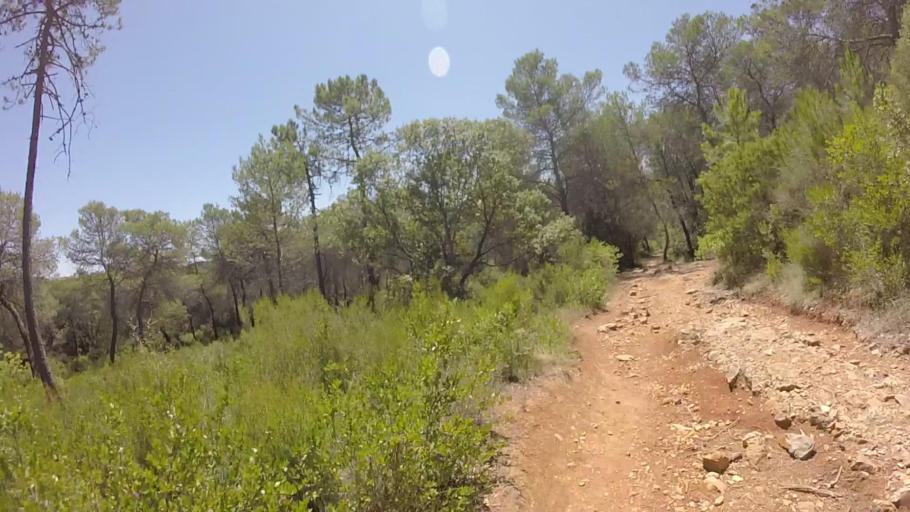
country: FR
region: Provence-Alpes-Cote d'Azur
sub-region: Departement des Alpes-Maritimes
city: Vallauris
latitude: 43.6114
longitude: 7.0477
